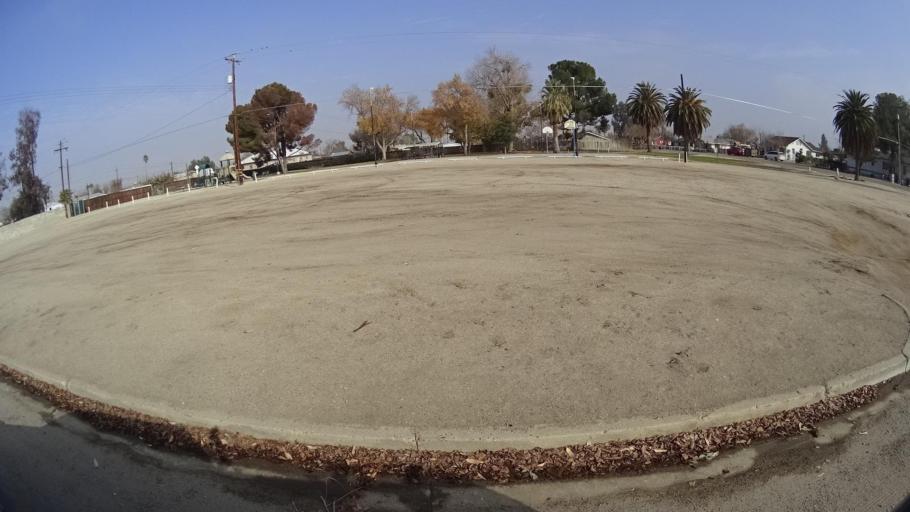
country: US
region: California
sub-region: Kern County
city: Ford City
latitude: 35.2064
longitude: -119.4072
